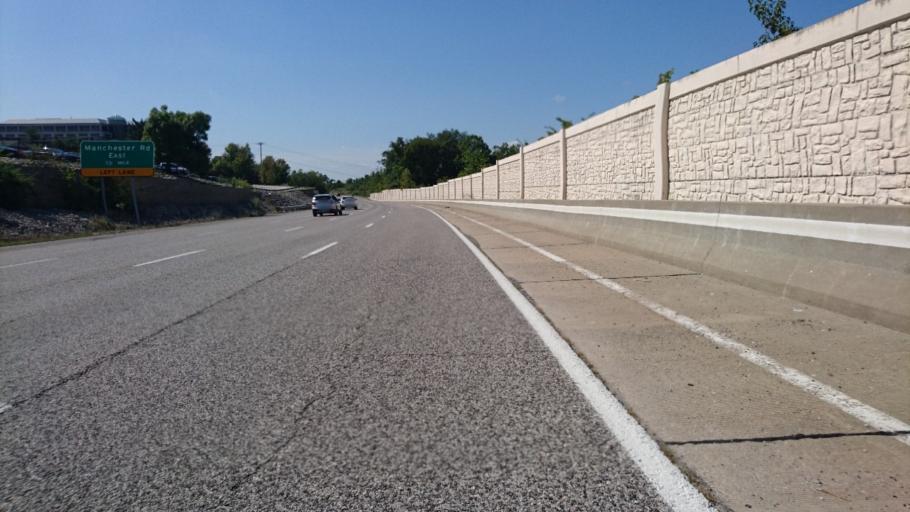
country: US
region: Missouri
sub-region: Saint Louis County
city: Town and Country
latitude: 38.6043
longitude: -90.4608
